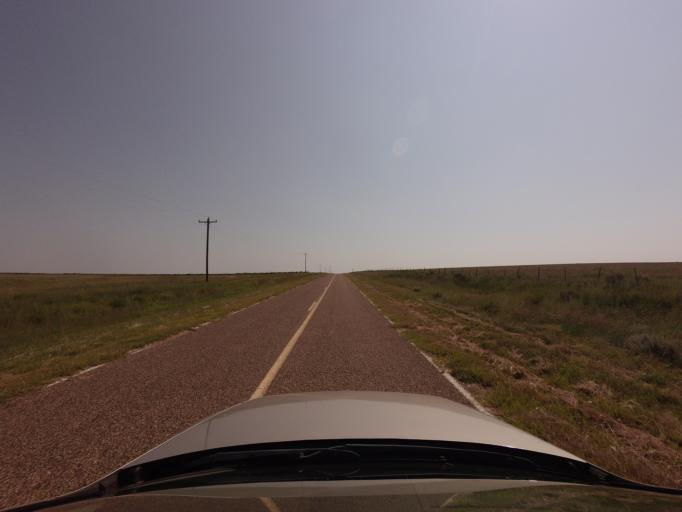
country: US
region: New Mexico
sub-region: Curry County
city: Cannon Air Force Base
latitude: 34.6335
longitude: -103.5847
